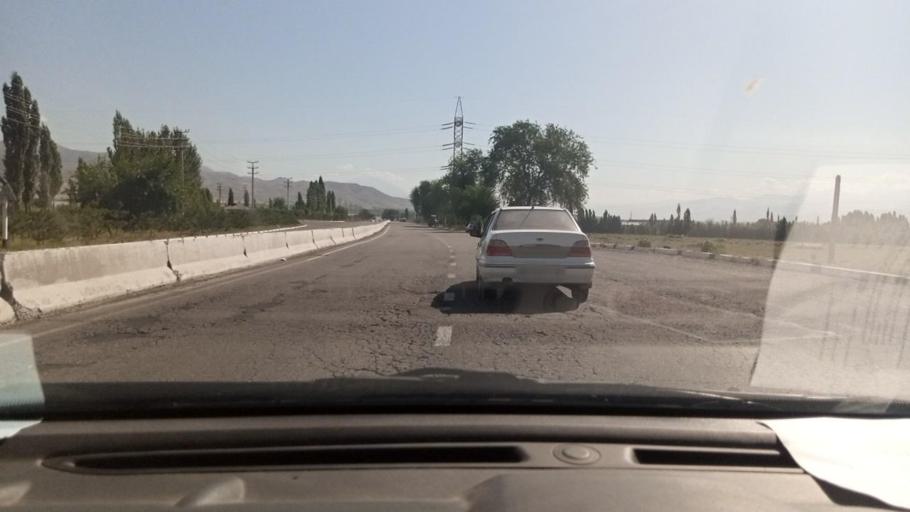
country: UZ
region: Toshkent
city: Ohangaron
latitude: 40.9156
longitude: 69.8287
